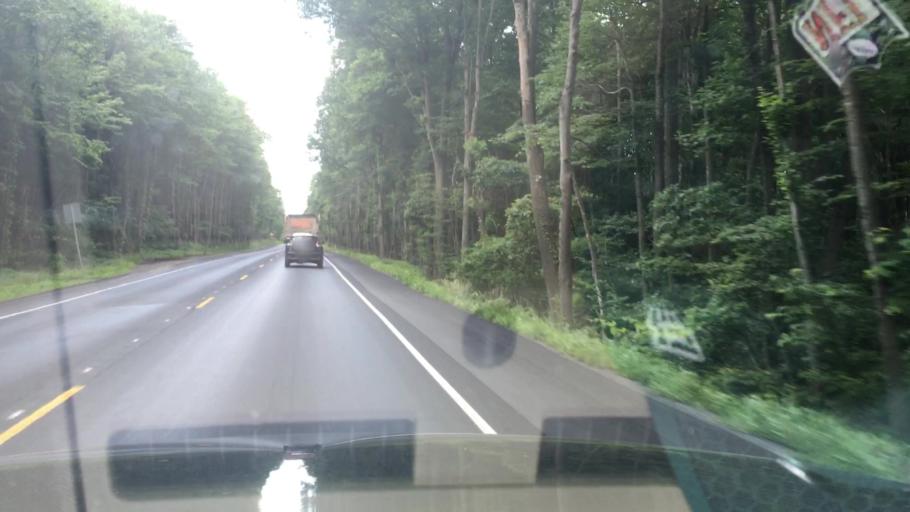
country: US
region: Pennsylvania
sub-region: Northumberland County
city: Mount Carmel
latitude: 40.7680
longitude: -76.4178
